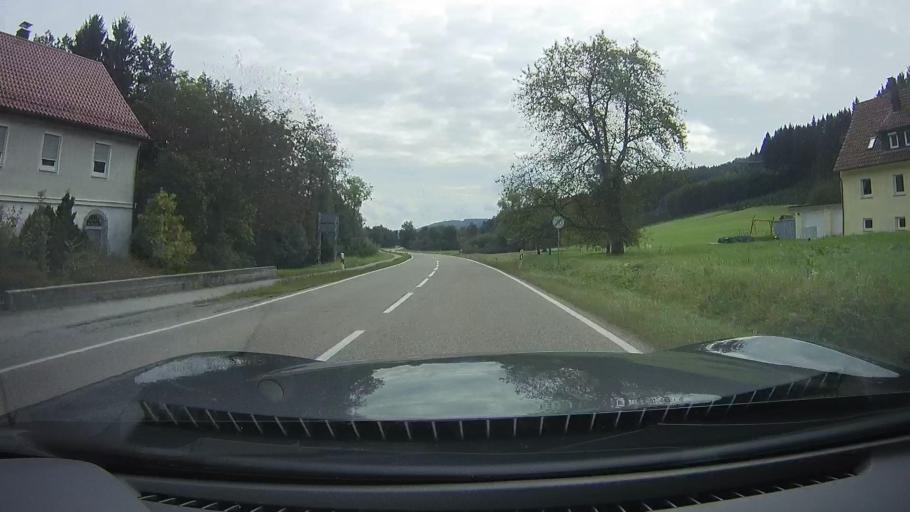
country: DE
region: Baden-Wuerttemberg
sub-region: Regierungsbezirk Stuttgart
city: Spiegelberg
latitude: 49.0194
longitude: 9.4613
